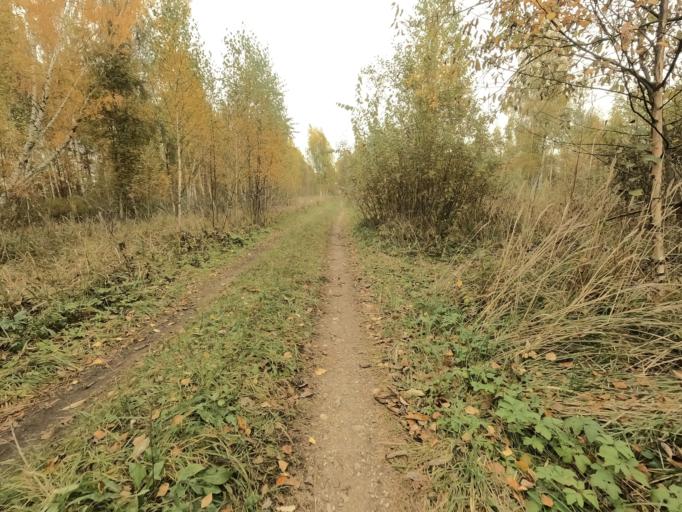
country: RU
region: Novgorod
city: Pankovka
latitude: 58.8767
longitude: 30.9406
